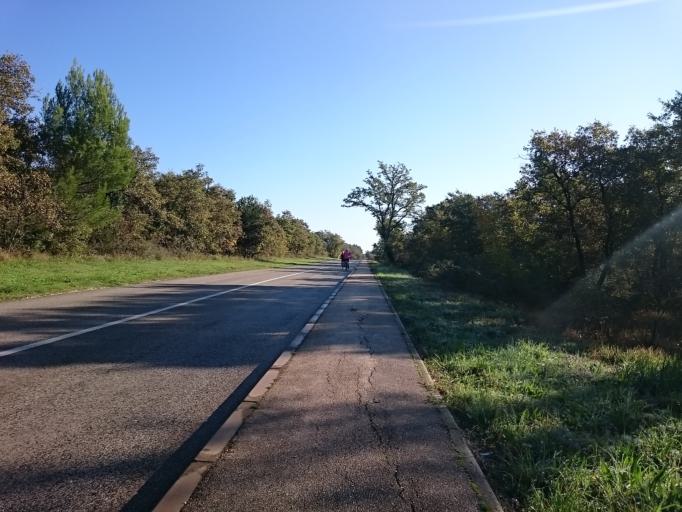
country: HR
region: Istarska
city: Novigrad
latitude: 45.3599
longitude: 13.5695
